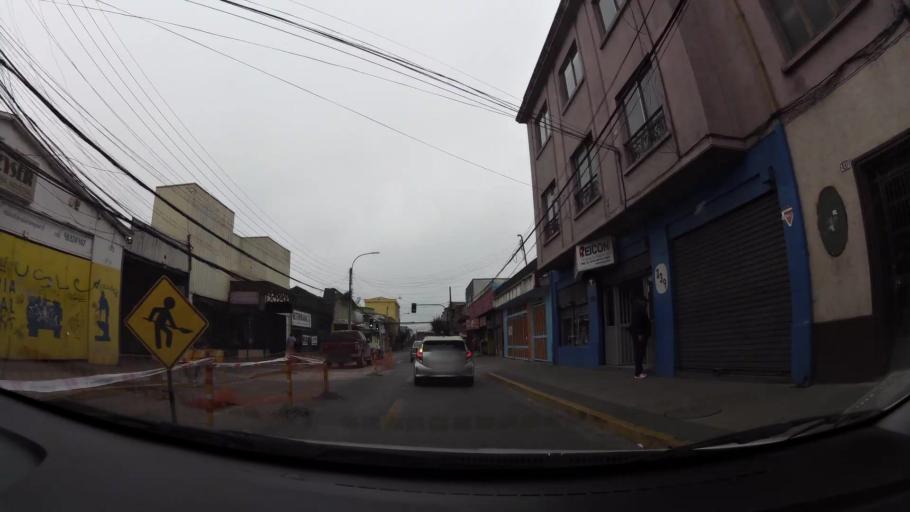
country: CL
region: Biobio
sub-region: Provincia de Concepcion
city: Concepcion
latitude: -36.8271
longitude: -73.0550
